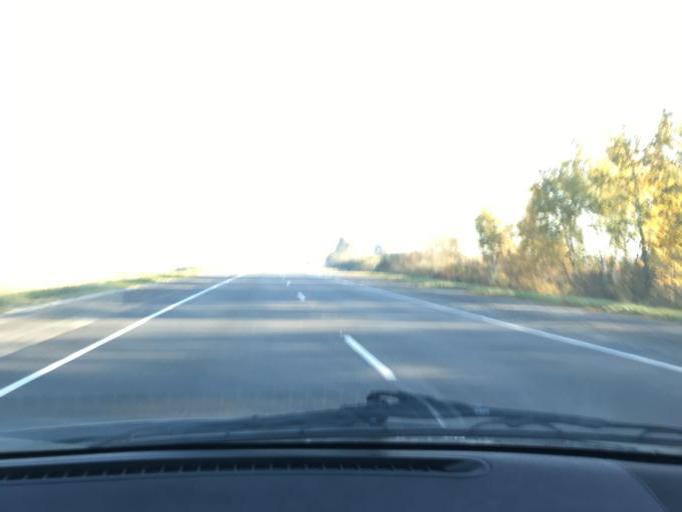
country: BY
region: Brest
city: Asnyezhytsy
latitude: 52.2226
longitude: 26.1329
